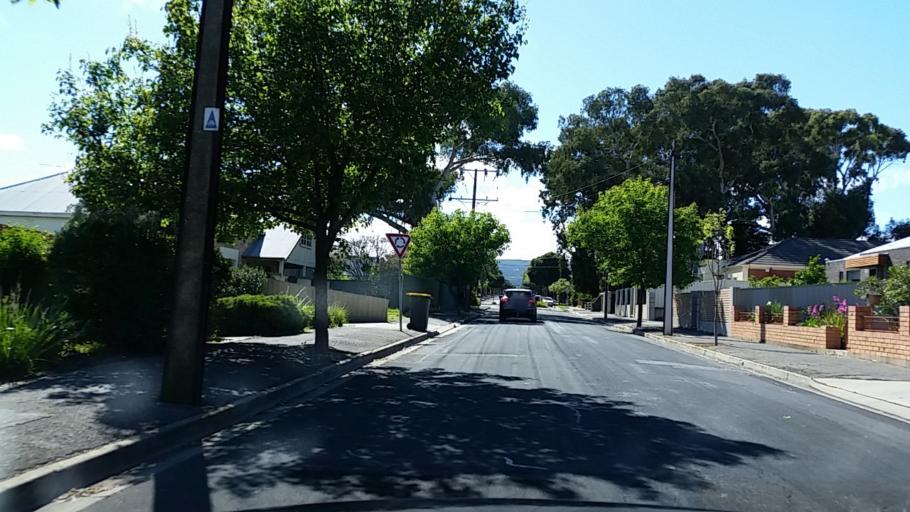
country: AU
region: South Australia
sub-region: Norwood Payneham St Peters
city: Payneham
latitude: -34.9014
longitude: 138.6474
